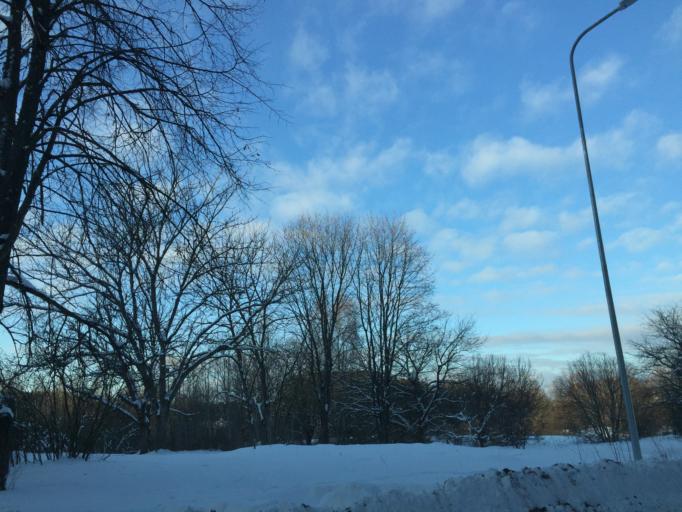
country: LV
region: Incukalns
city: Incukalns
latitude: 57.1033
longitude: 24.6750
